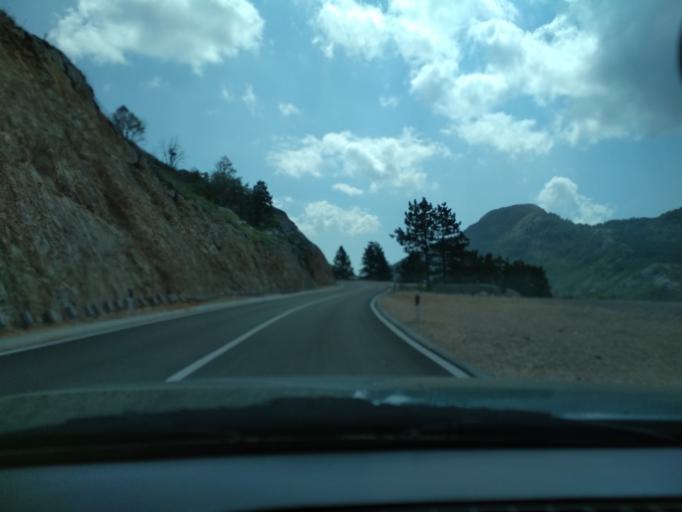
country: ME
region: Kotor
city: Kotor
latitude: 42.4369
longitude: 18.8430
